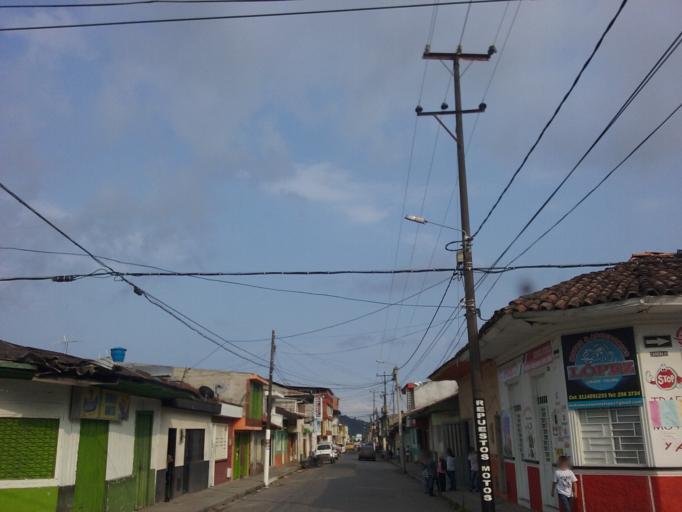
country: CO
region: Tolima
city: Libano
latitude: 4.9216
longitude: -75.0664
